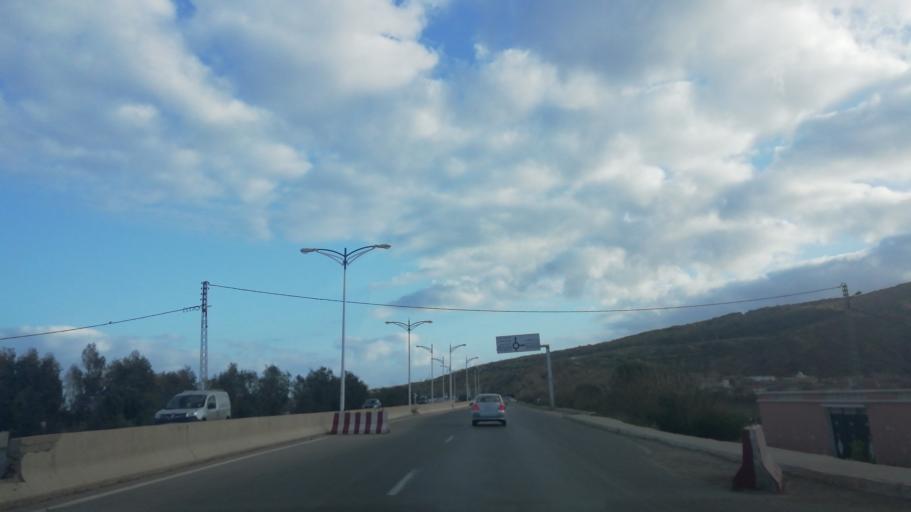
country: DZ
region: Mostaganem
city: Mostaganem
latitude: 36.0325
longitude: 0.1398
